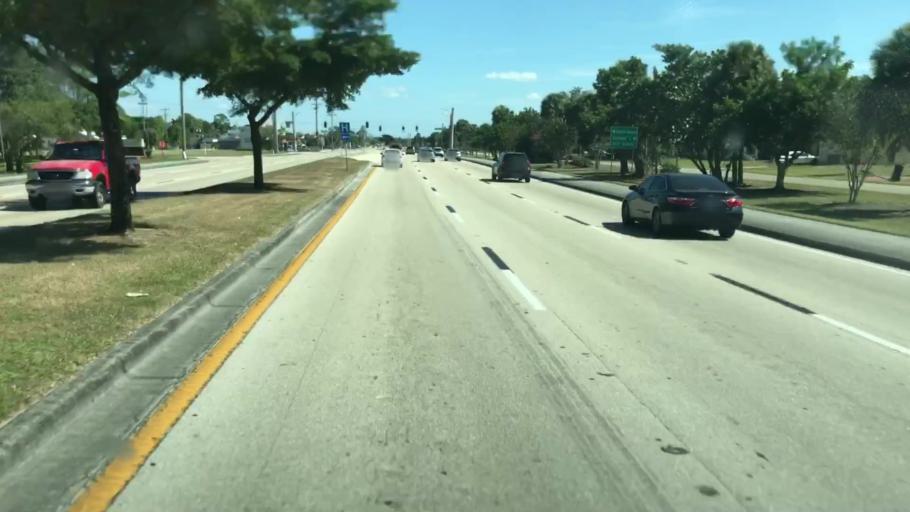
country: US
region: Florida
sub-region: Lee County
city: Lehigh Acres
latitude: 26.6141
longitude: -81.6604
